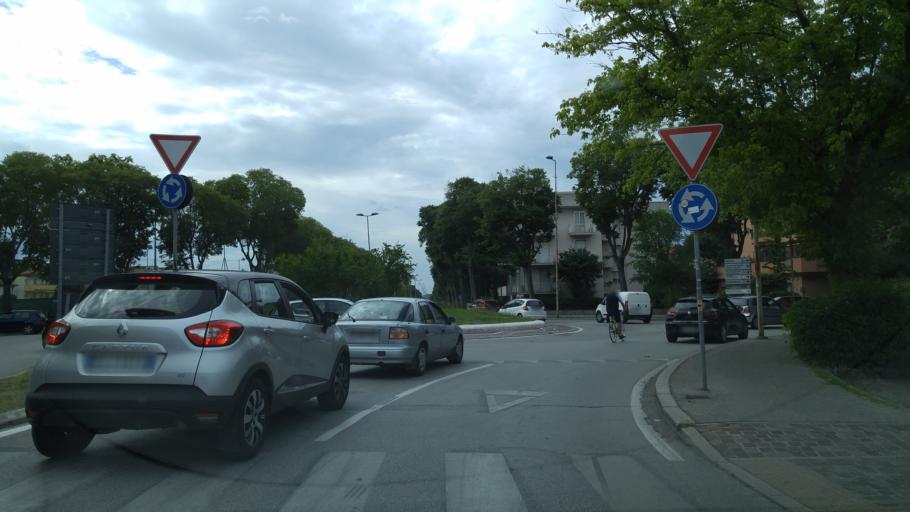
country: IT
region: Emilia-Romagna
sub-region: Provincia di Rimini
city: Rimini
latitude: 44.0467
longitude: 12.5637
